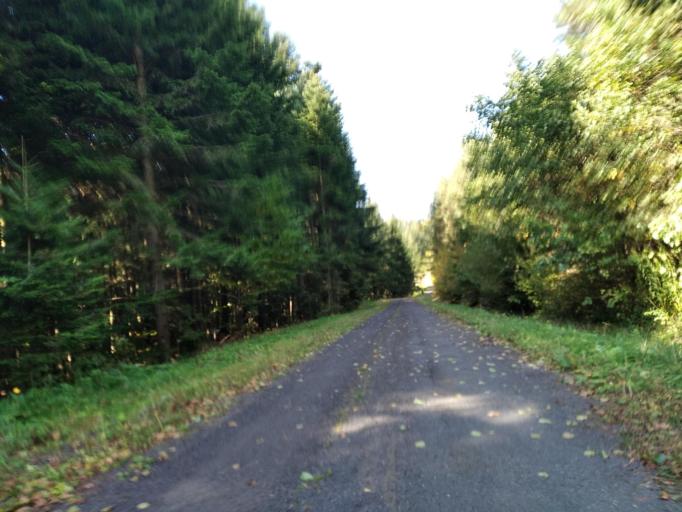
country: PL
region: Subcarpathian Voivodeship
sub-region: Powiat strzyzowski
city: Strzyzow
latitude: 49.8125
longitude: 21.7999
